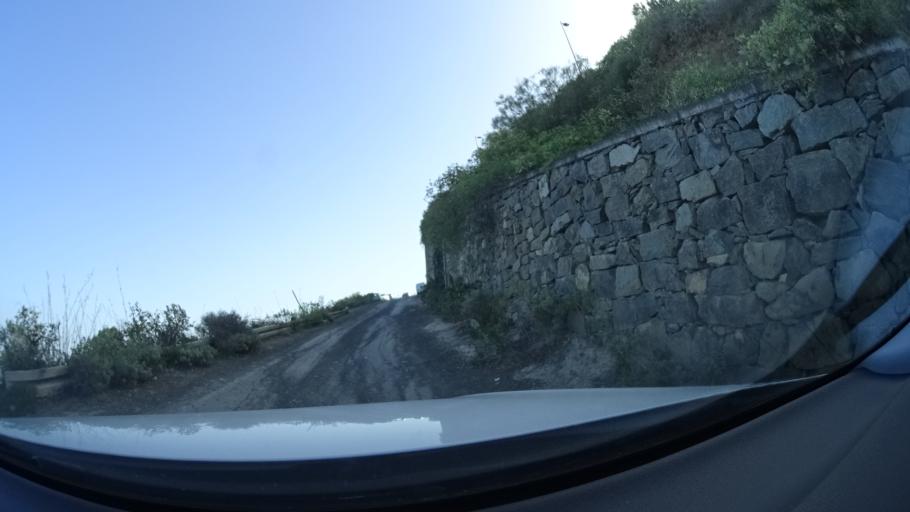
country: ES
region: Canary Islands
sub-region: Provincia de Las Palmas
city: Santa Brigida
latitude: 28.0324
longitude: -15.4596
